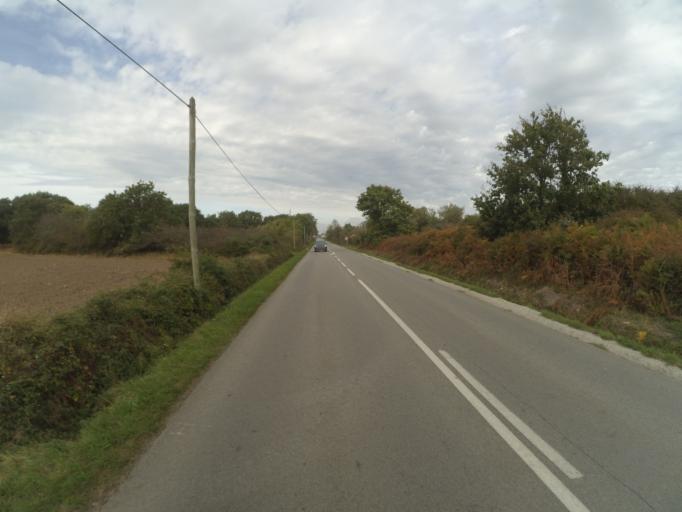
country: FR
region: Brittany
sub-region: Departement du Morbihan
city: Belz
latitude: 47.6625
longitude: -3.1753
